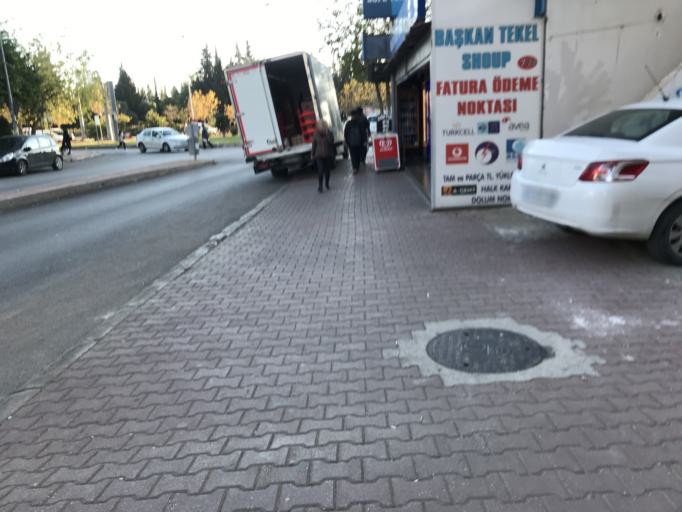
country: TR
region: Antalya
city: Antalya
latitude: 36.8960
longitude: 30.7072
